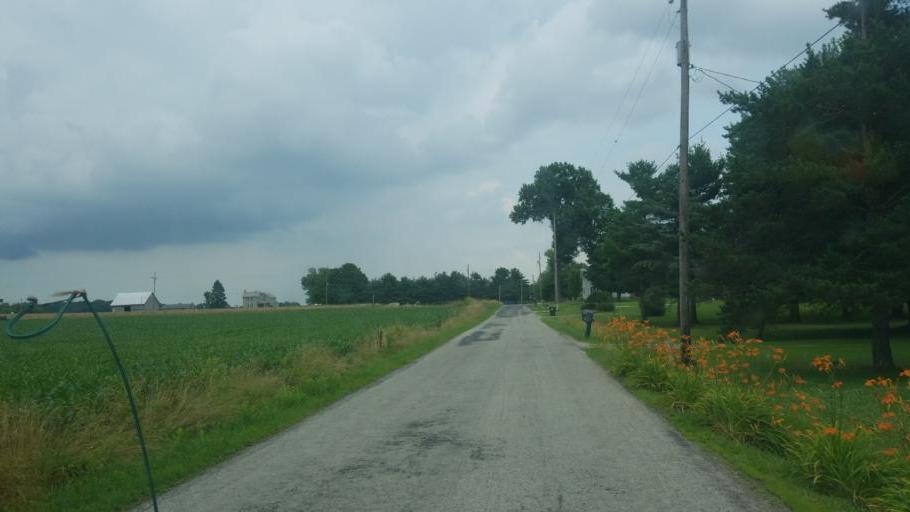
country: US
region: Ohio
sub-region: Wayne County
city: Smithville
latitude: 40.8944
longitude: -81.9009
